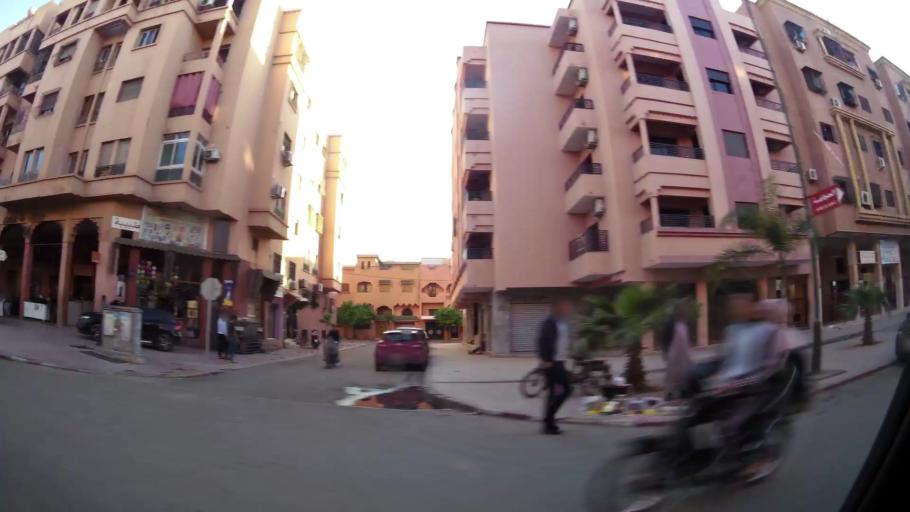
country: MA
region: Marrakech-Tensift-Al Haouz
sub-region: Marrakech
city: Marrakesh
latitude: 31.6227
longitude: -8.0289
